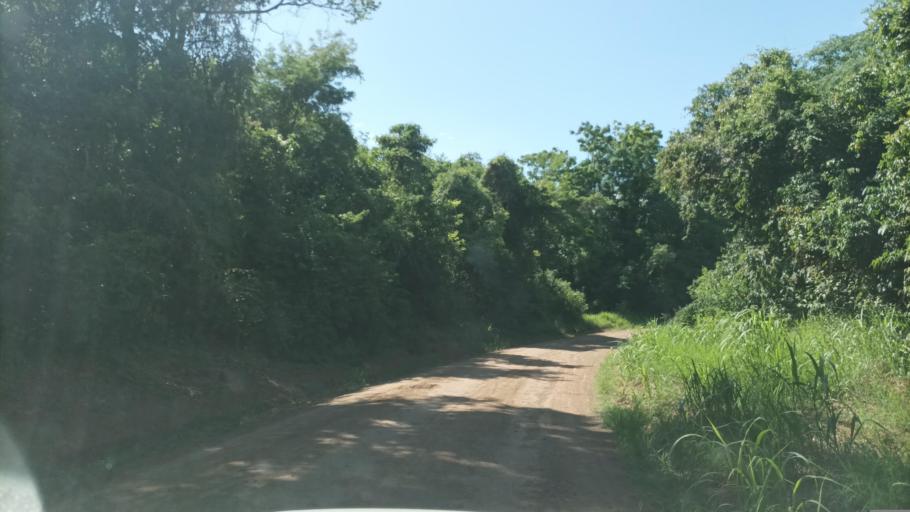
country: AR
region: Misiones
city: Cerro Cora
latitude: -27.5147
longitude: -55.5518
